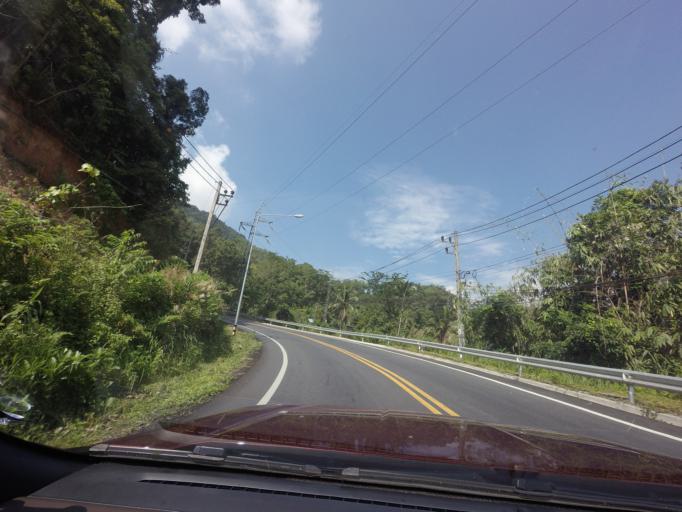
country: TH
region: Yala
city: Betong
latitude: 5.9085
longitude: 101.1507
